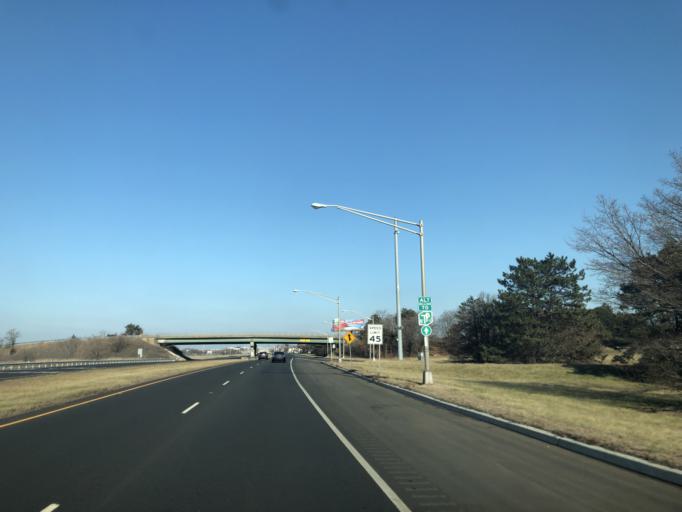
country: US
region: New Jersey
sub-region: Hudson County
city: Bayonne
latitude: 40.6947
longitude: -74.1084
